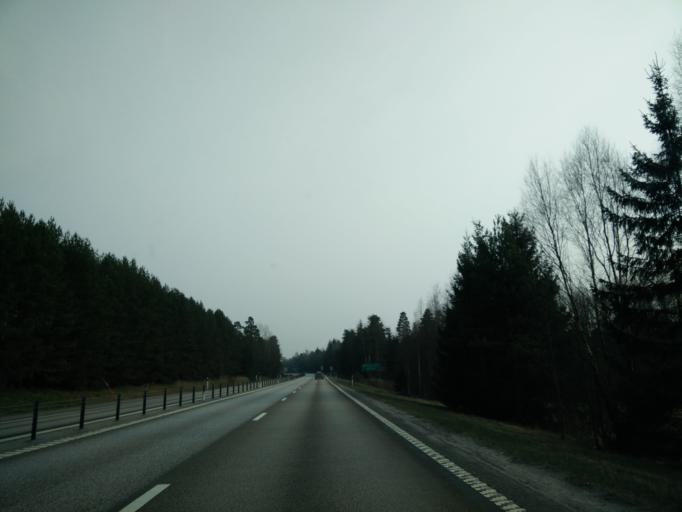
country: SE
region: Vaermland
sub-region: Hammaro Kommun
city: Skoghall
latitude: 59.3895
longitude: 13.4214
